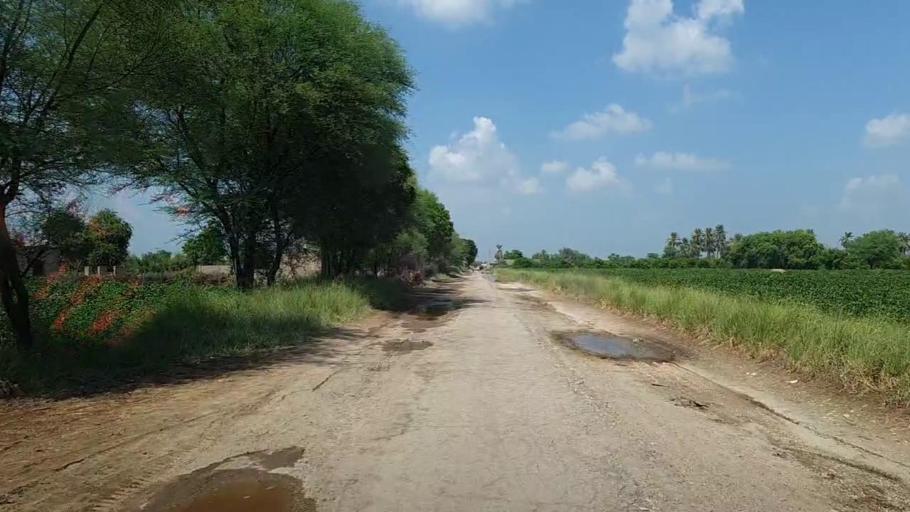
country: PK
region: Sindh
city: Kandiaro
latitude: 27.0253
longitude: 68.2743
